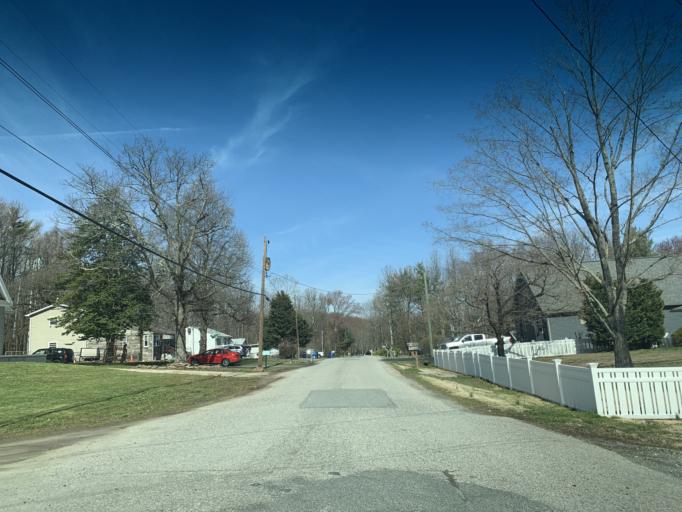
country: US
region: Maryland
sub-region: Cecil County
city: Charlestown
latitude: 39.5439
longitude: -76.0068
